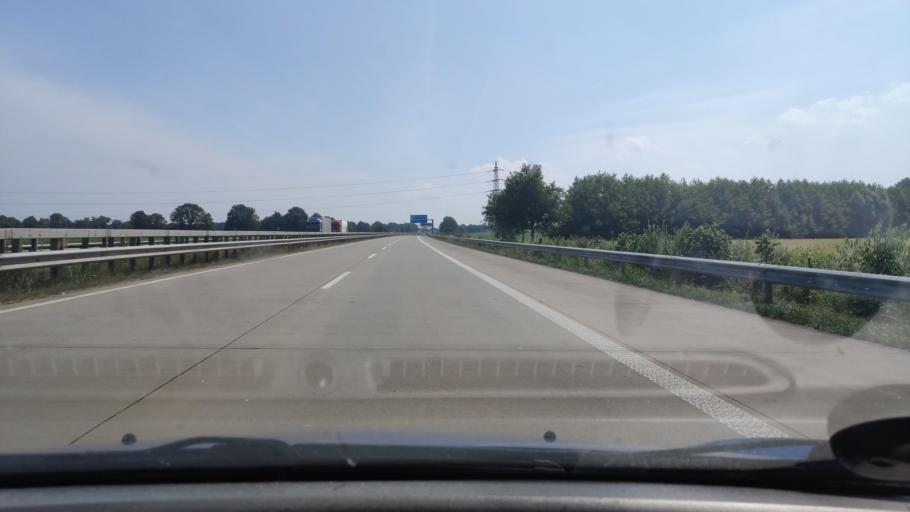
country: DE
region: Lower Saxony
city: Quendorf
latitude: 52.3424
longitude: 7.2031
